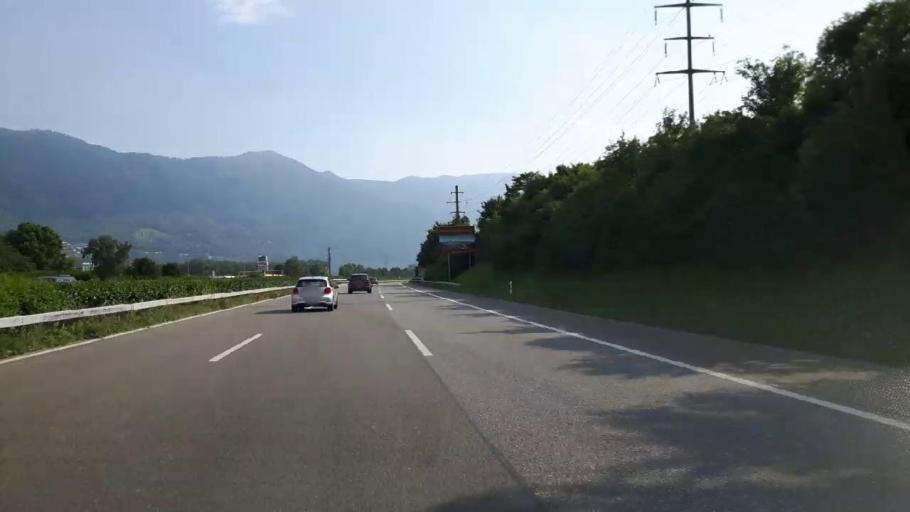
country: CH
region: Ticino
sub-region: Bellinzona District
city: Monte Carasso
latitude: 46.1848
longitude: 9.0029
